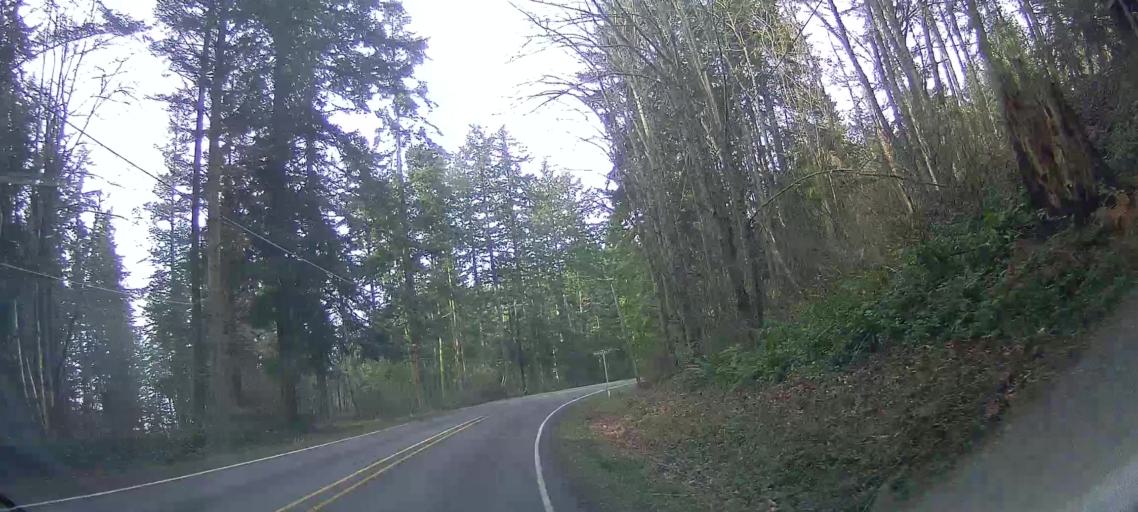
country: US
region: Washington
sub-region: Island County
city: Camano
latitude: 48.2006
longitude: -122.5324
